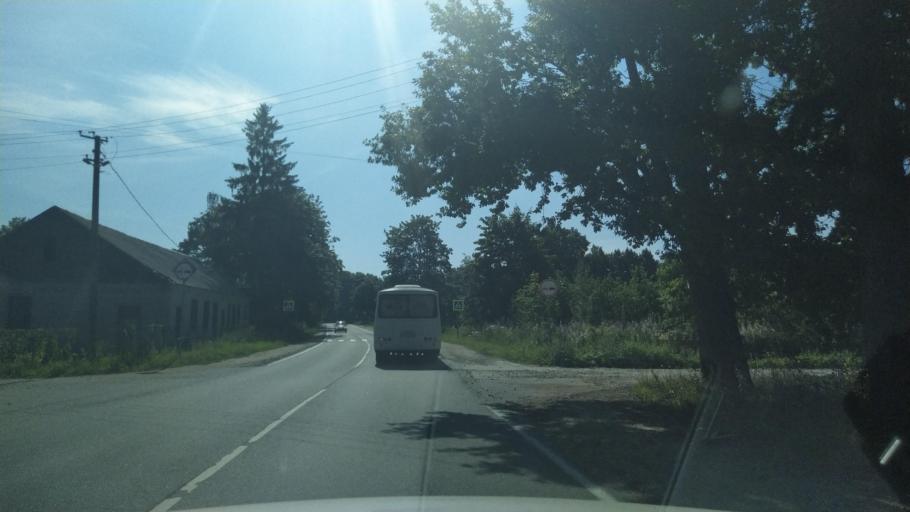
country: RU
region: Leningrad
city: Siverskiy
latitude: 59.3185
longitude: 30.0696
